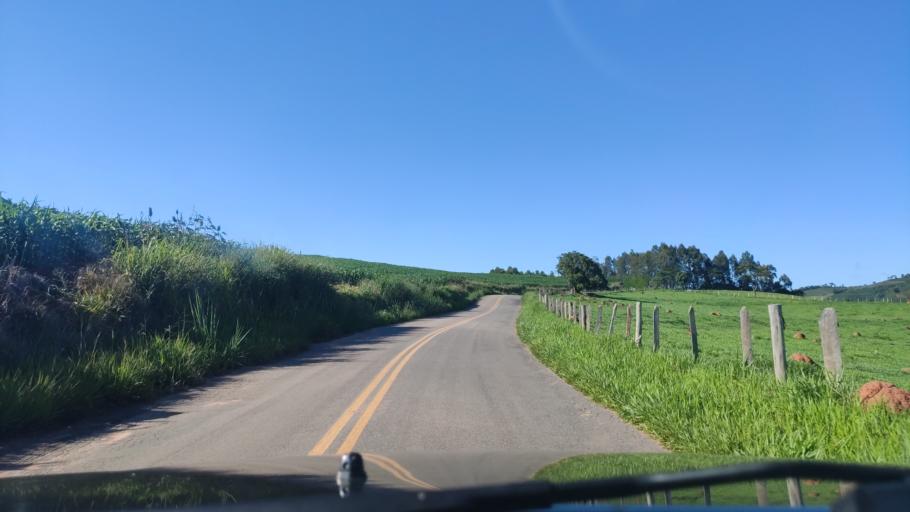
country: BR
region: Sao Paulo
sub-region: Aguas De Lindoia
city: Aguas de Lindoia
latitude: -22.5575
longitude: -46.6199
